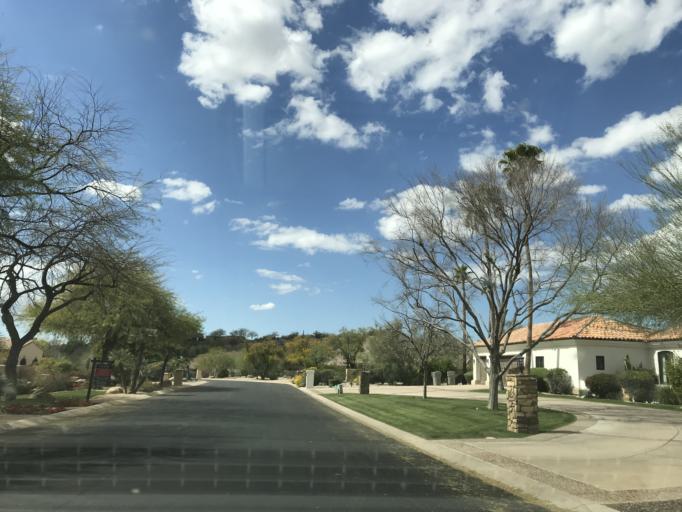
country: US
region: Arizona
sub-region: Maricopa County
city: Paradise Valley
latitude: 33.5212
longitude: -112.0101
